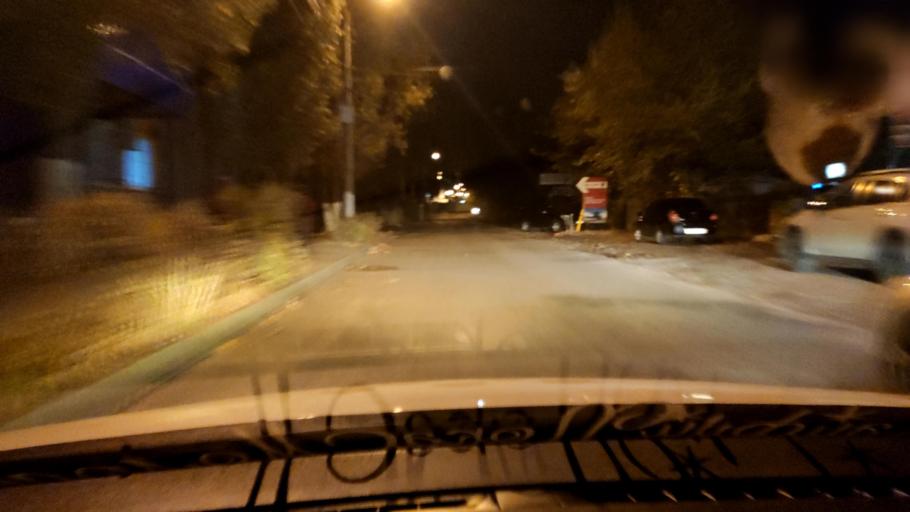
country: RU
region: Voronezj
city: Voronezh
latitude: 51.6611
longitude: 39.1343
